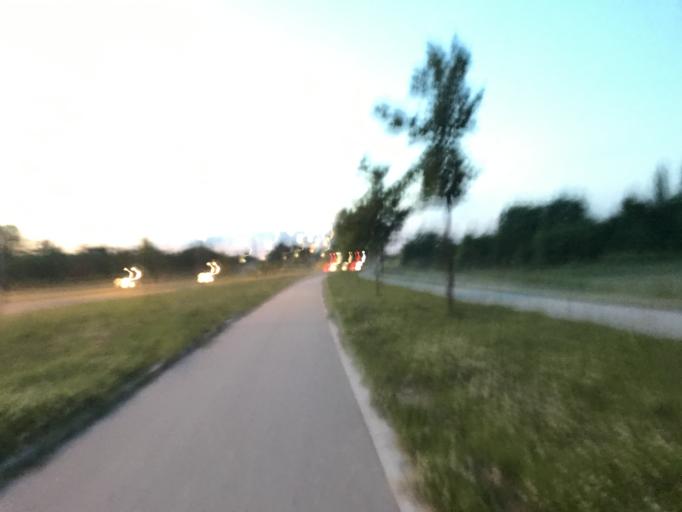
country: RS
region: Autonomna Pokrajina Vojvodina
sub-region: Juznobacki Okrug
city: Novi Sad
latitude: 45.2726
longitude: 19.8010
